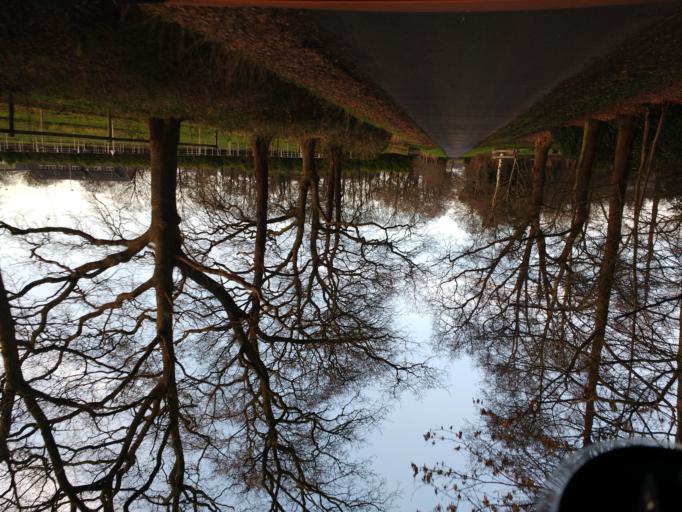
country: DE
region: Lower Saxony
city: Hatten
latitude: 53.1189
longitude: 8.3643
